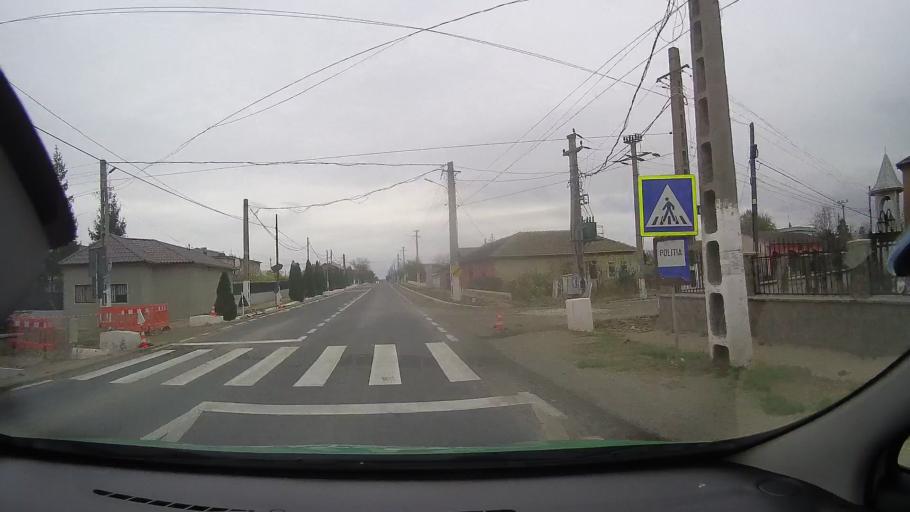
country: RO
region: Constanta
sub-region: Comuna Nicolae Balcescu
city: Nicolae Balcescu
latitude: 44.3880
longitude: 28.3810
